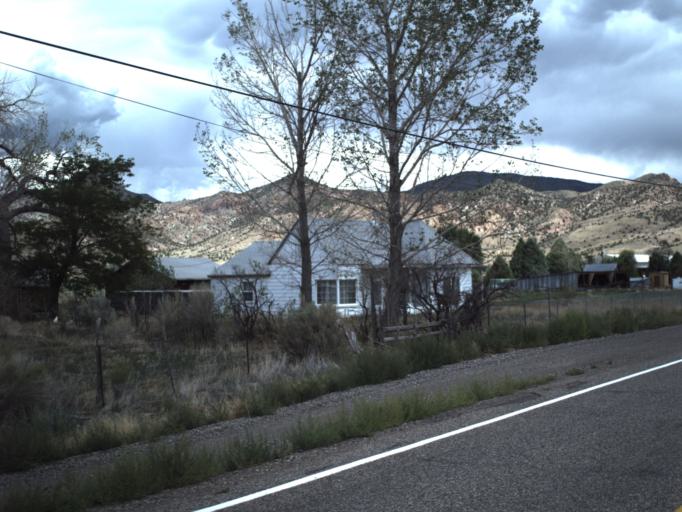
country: US
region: Utah
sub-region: Piute County
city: Junction
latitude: 38.2083
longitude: -112.1904
